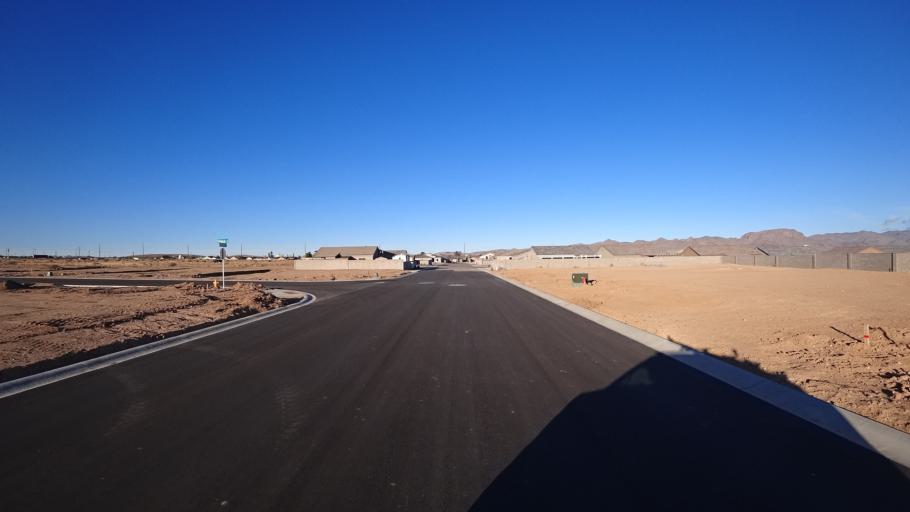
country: US
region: Arizona
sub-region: Mohave County
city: New Kingman-Butler
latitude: 35.2214
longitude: -113.9900
